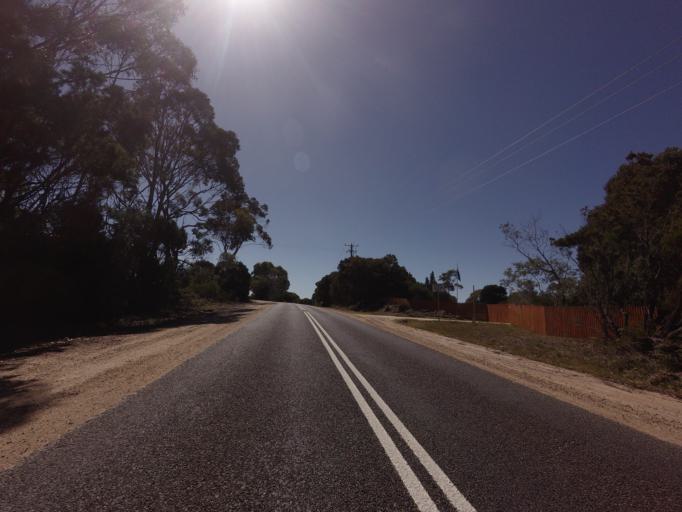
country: AU
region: Tasmania
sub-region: Break O'Day
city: St Helens
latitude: -41.8285
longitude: 148.2611
